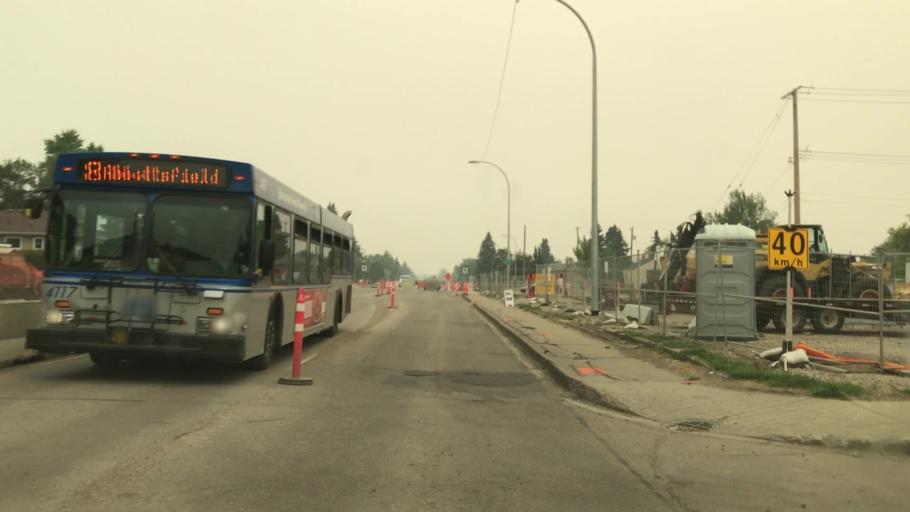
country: CA
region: Alberta
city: Edmonton
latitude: 53.5132
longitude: -113.4552
